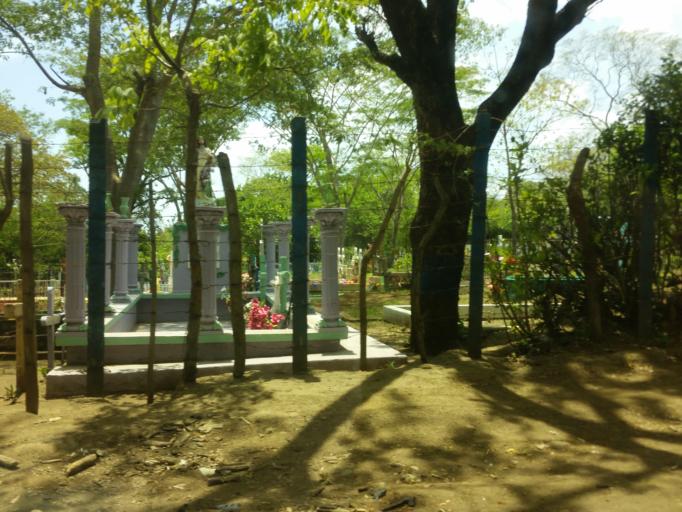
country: NI
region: Managua
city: Managua
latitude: 12.1001
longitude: -86.2740
